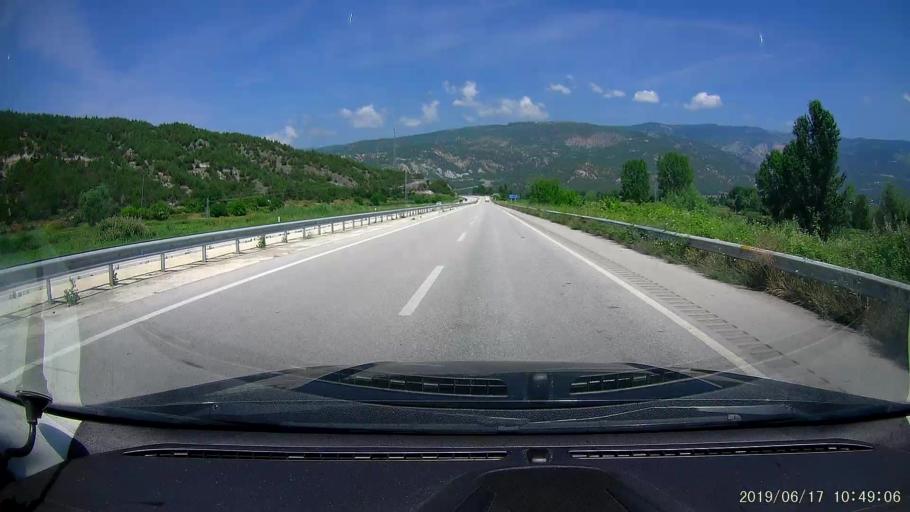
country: TR
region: Corum
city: Hacihamza
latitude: 41.0977
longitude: 34.4170
